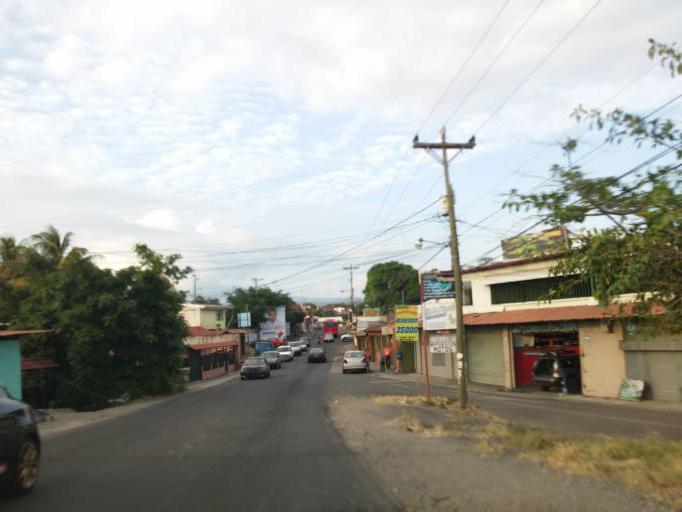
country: CR
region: Alajuela
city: Alajuela
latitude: 10.0000
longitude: -84.2197
